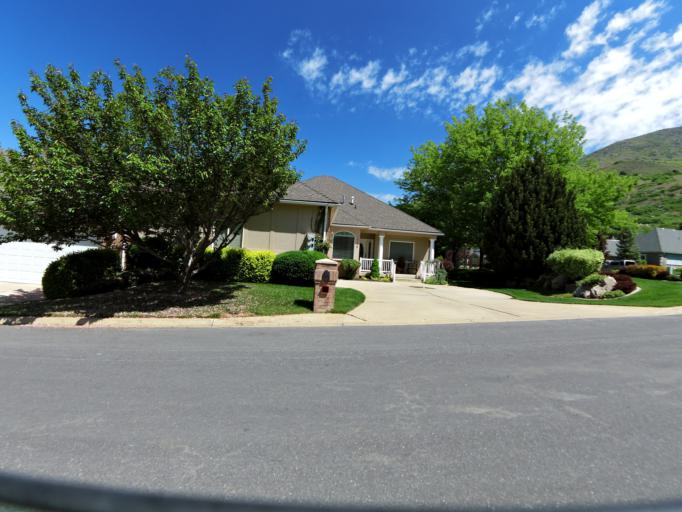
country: US
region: Utah
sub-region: Weber County
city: Uintah
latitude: 41.1763
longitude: -111.9325
